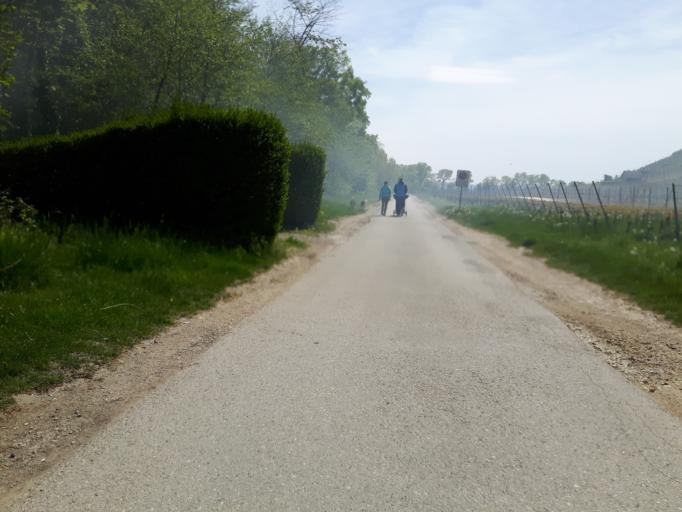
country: CH
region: Neuchatel
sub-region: Boudry District
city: Cortaillod
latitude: 46.9303
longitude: 6.8380
